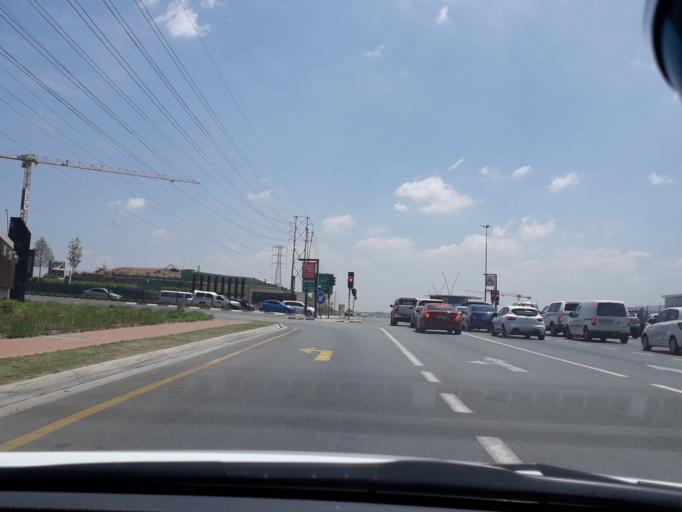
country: ZA
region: Gauteng
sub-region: City of Johannesburg Metropolitan Municipality
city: Midrand
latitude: -26.0128
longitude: 28.1096
